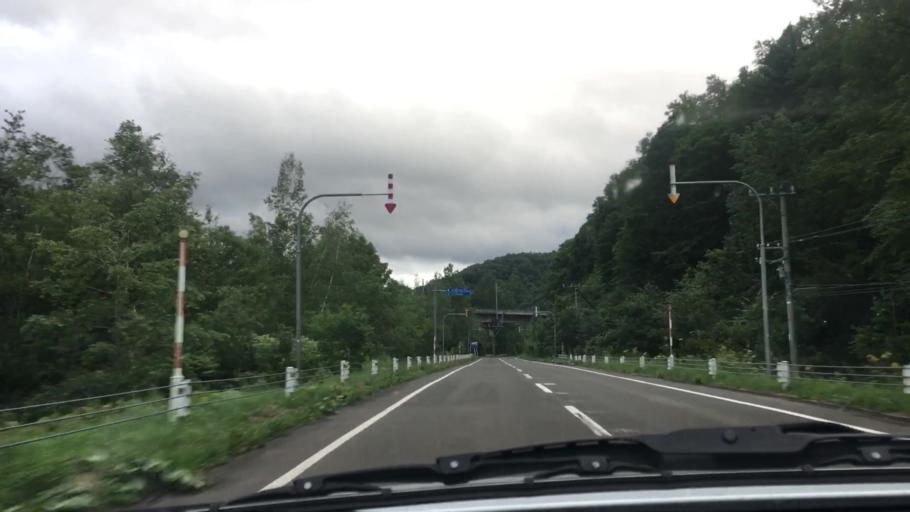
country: JP
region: Hokkaido
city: Shimo-furano
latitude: 43.0644
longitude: 142.5316
